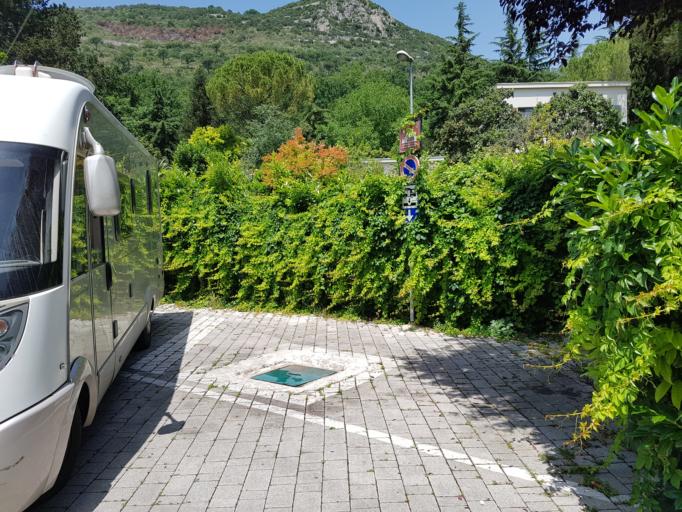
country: IT
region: Latium
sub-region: Provincia di Frosinone
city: Cassino
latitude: 41.4831
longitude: 13.8222
